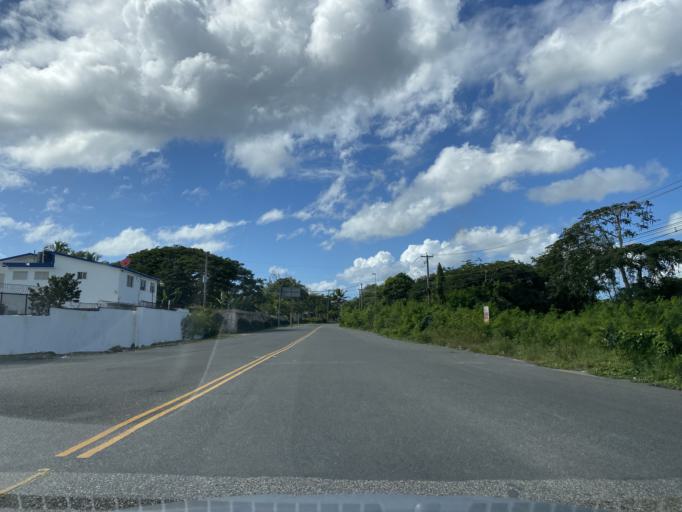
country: DO
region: Santo Domingo
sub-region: Santo Domingo
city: Boca Chica
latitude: 18.4495
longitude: -69.5973
